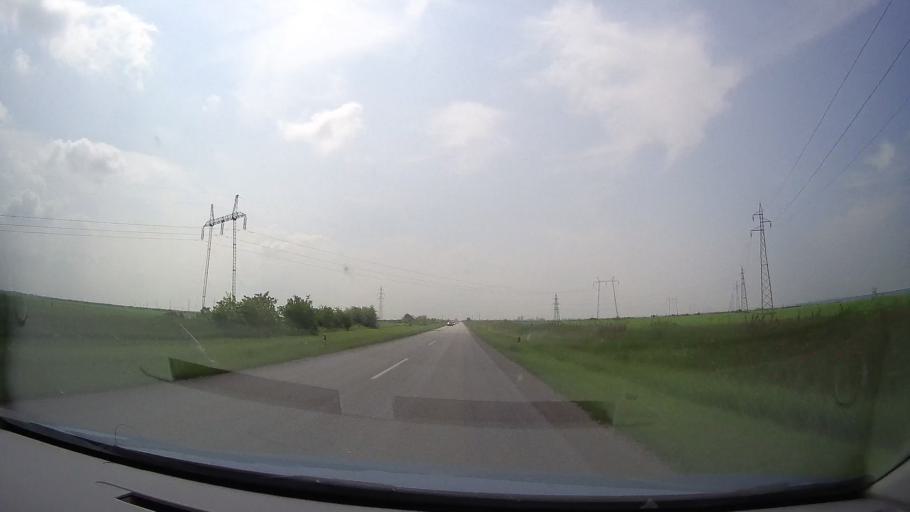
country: RS
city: Crepaja
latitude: 44.9683
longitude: 20.6519
